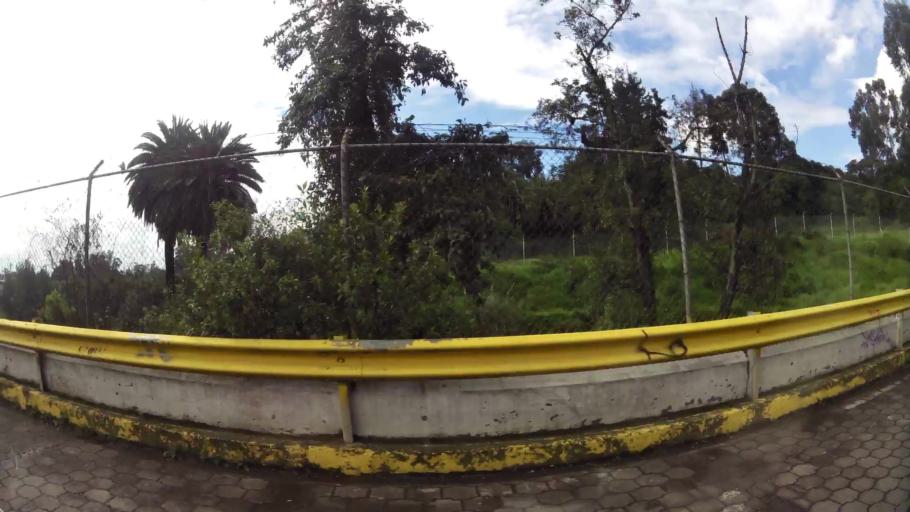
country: EC
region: Pichincha
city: Sangolqui
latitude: -0.3338
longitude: -78.4401
